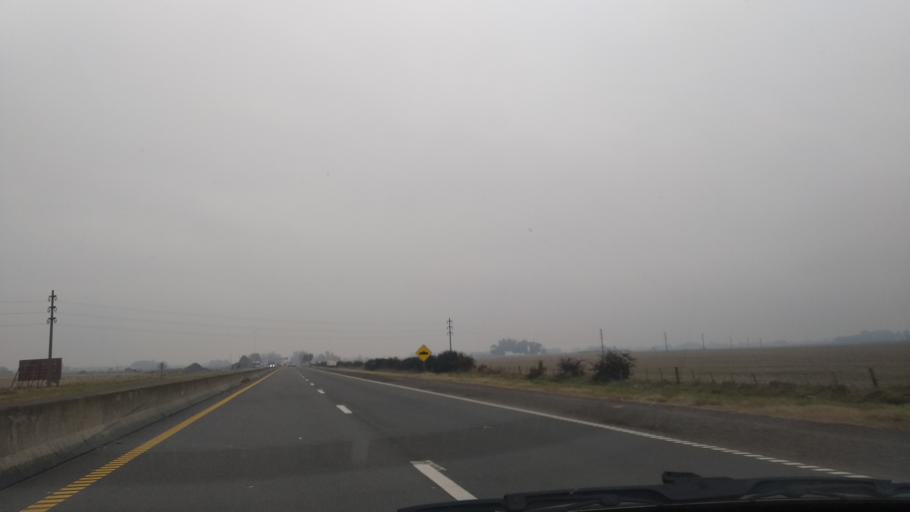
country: AR
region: Buenos Aires
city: Olavarria
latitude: -36.8576
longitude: -60.1177
